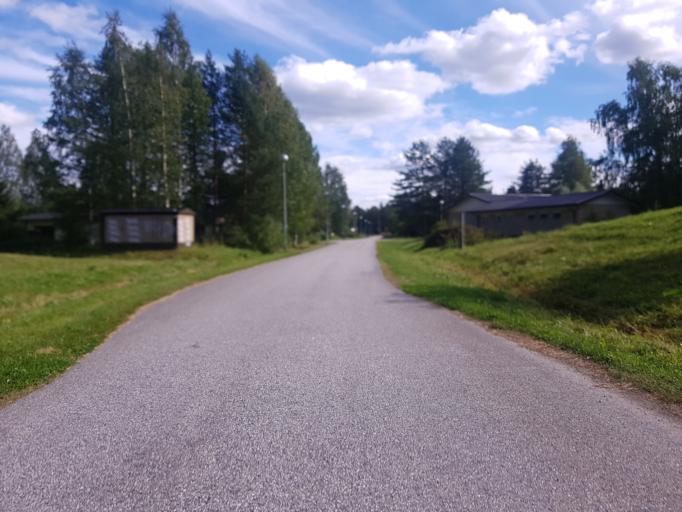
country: FI
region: Kainuu
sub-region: Kehys-Kainuu
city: Kuhmo
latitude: 64.1234
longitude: 29.5252
